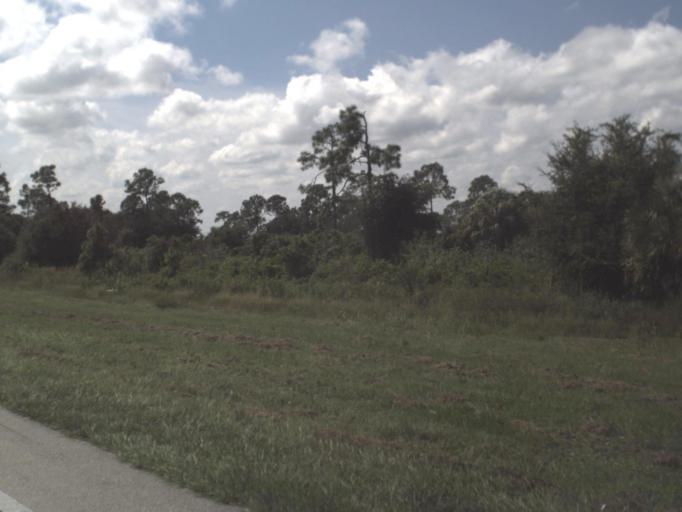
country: US
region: Florida
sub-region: Collier County
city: Immokalee
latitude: 26.5087
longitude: -81.4350
